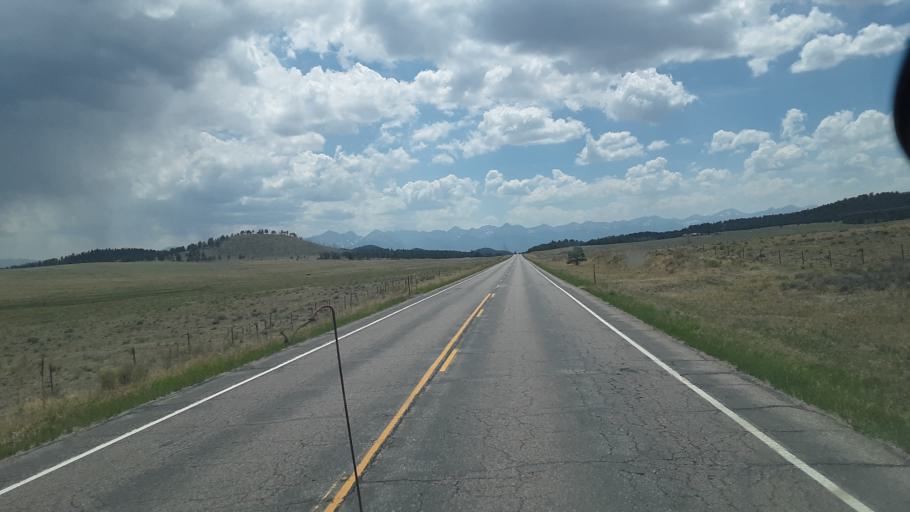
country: US
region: Colorado
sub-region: Custer County
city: Westcliffe
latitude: 38.1623
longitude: -105.2918
